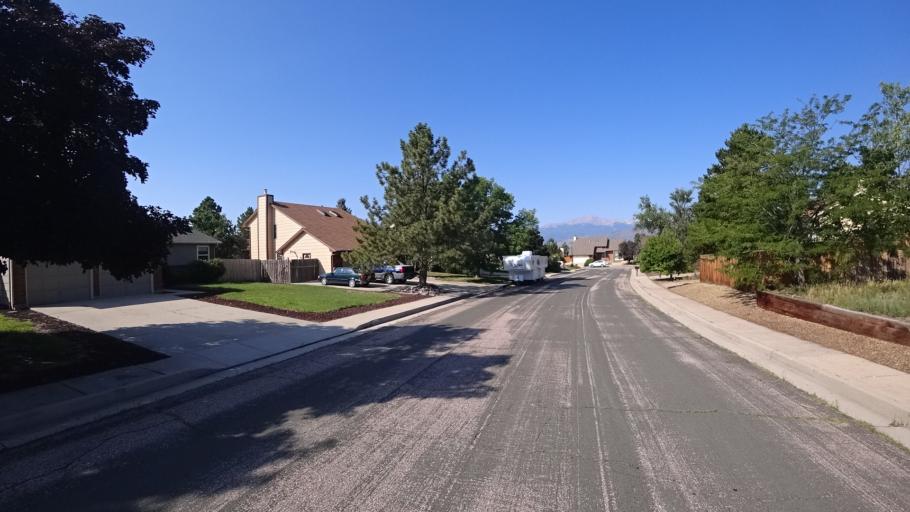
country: US
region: Colorado
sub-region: El Paso County
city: Air Force Academy
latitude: 38.9545
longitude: -104.7849
